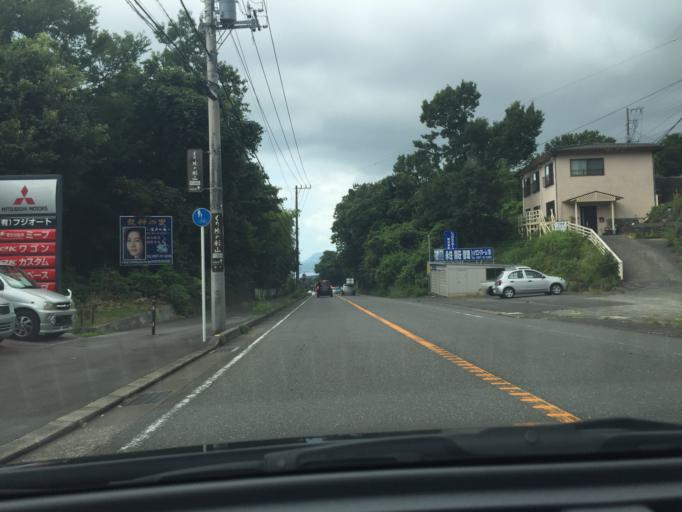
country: JP
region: Shizuoka
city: Ito
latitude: 34.8943
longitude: 139.1187
